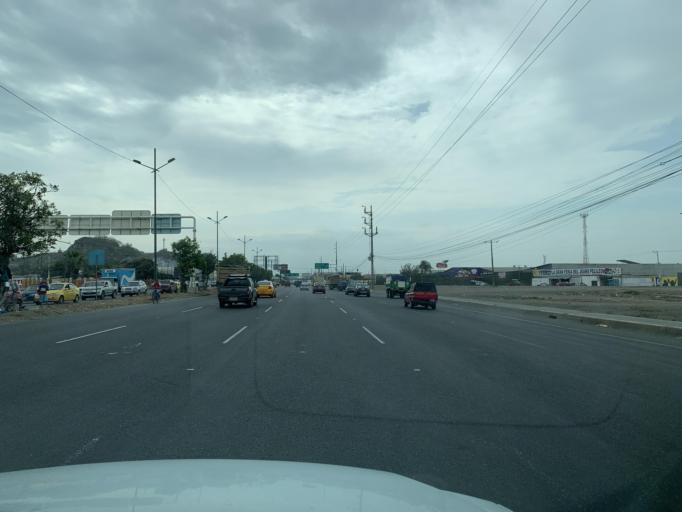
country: EC
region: Guayas
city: Eloy Alfaro
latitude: -2.1745
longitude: -79.8314
